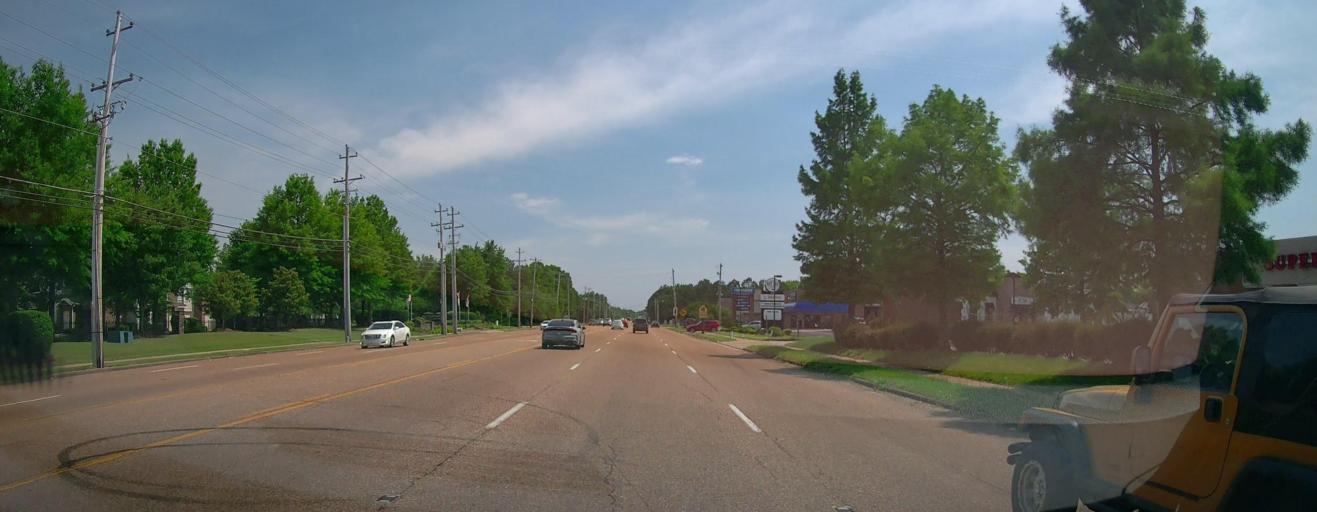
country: US
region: Tennessee
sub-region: Shelby County
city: Germantown
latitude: 35.0329
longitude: -89.7959
